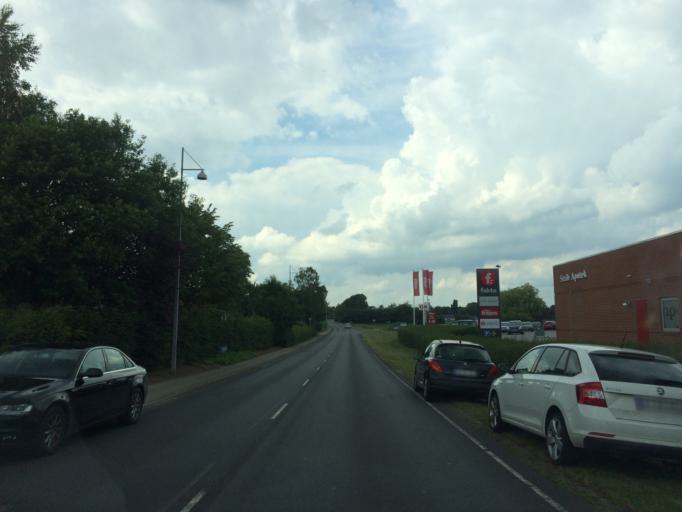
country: DK
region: South Denmark
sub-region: Middelfart Kommune
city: Strib
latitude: 55.5320
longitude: 9.7763
